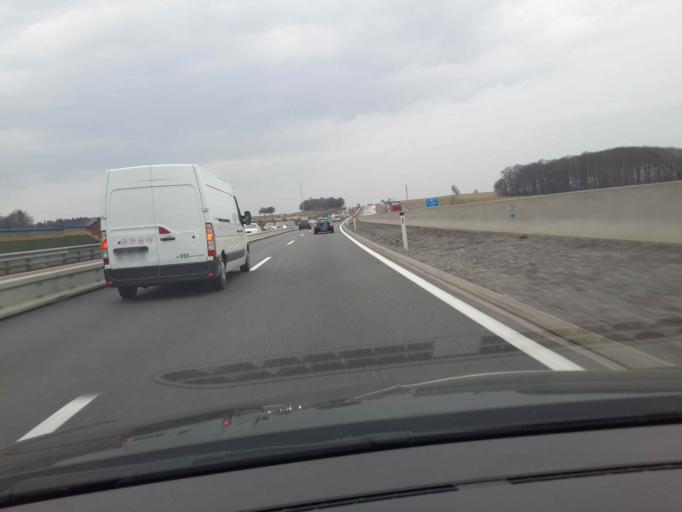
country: AT
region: Lower Austria
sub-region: Politischer Bezirk Sankt Polten
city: Pyhra
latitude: 48.1850
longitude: 15.7003
